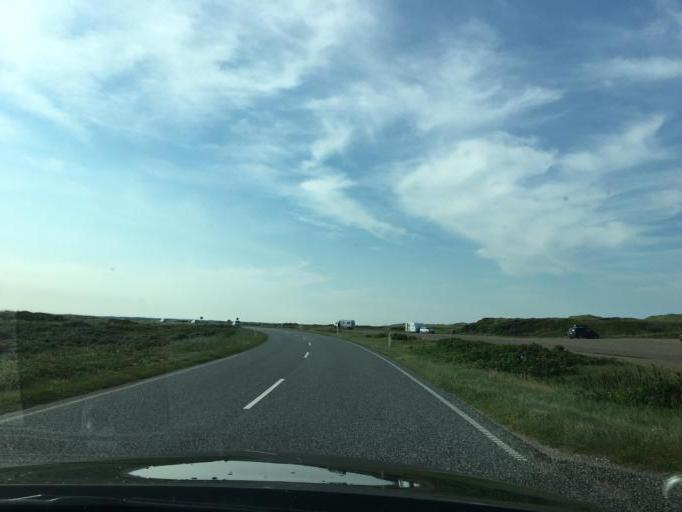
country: DK
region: Central Jutland
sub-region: Ringkobing-Skjern Kommune
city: Hvide Sande
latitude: 55.8278
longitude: 8.1726
